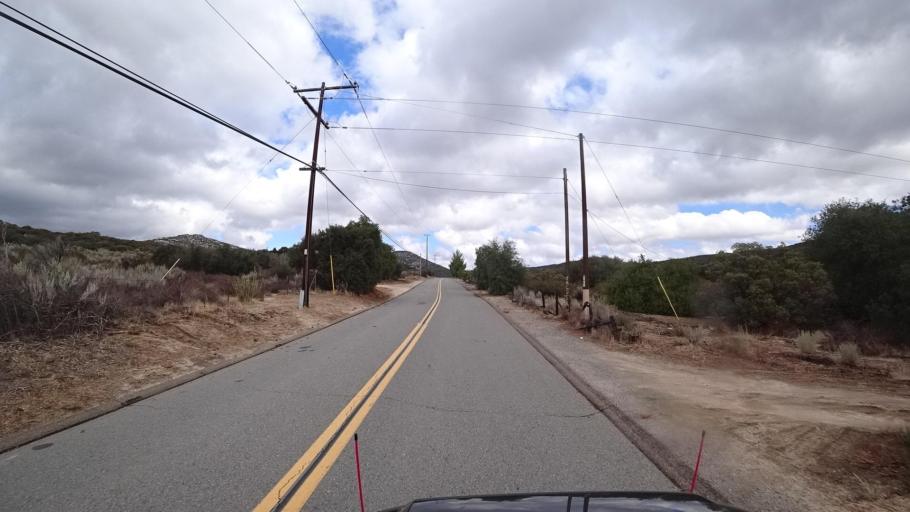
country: US
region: California
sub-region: San Diego County
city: Campo
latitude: 32.6555
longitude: -116.4250
